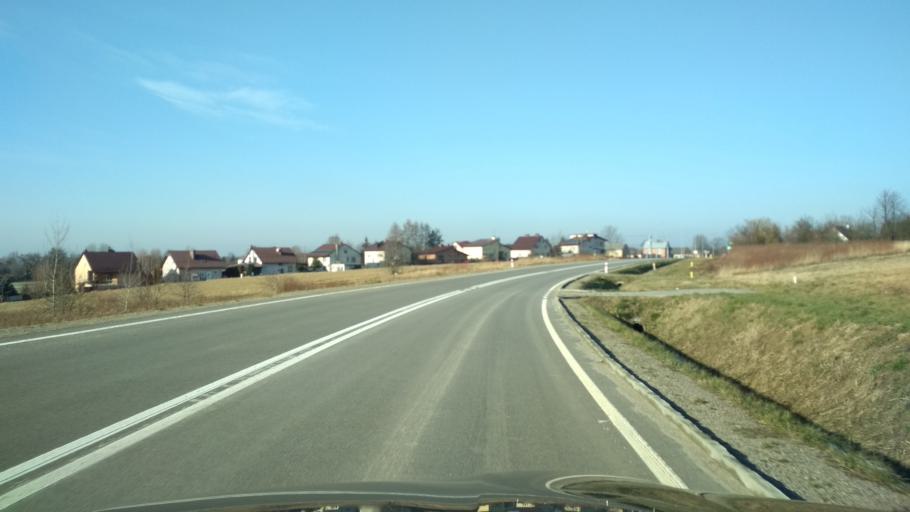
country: PL
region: Subcarpathian Voivodeship
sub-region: Powiat ropczycko-sedziszowski
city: Sedziszow Malopolski
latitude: 50.0783
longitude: 21.7241
